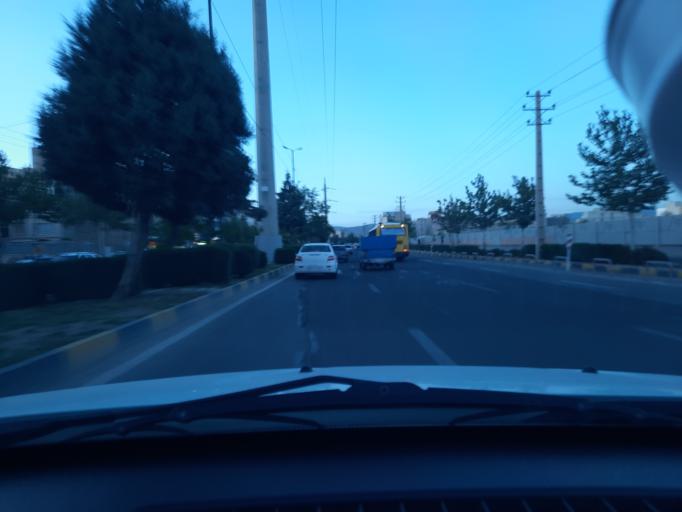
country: IR
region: Qazvin
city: Qazvin
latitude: 36.3031
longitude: 50.0107
